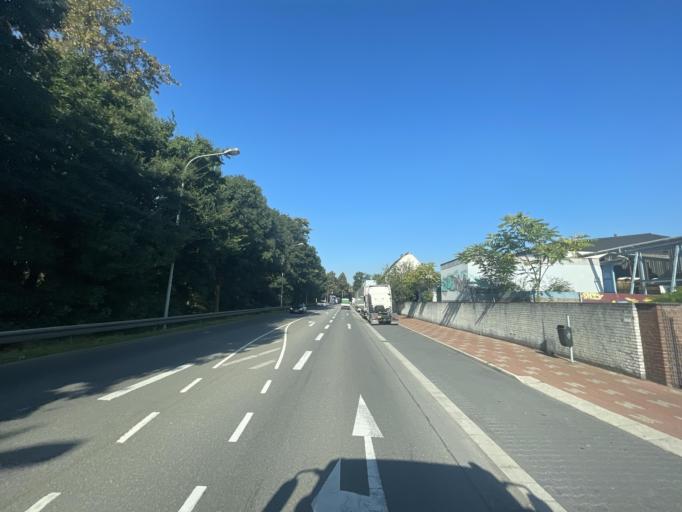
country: DE
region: North Rhine-Westphalia
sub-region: Regierungsbezirk Dusseldorf
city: Meerbusch
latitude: 51.3355
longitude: 6.6687
